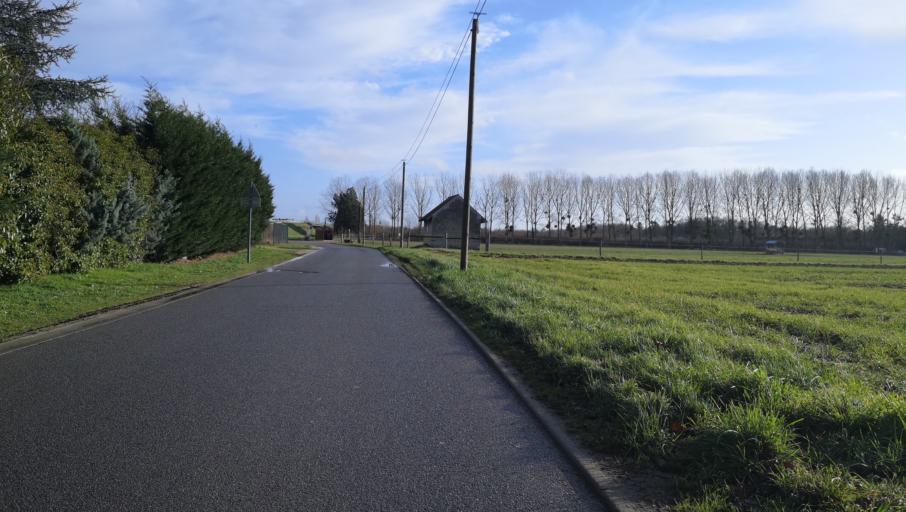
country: FR
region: Centre
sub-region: Departement du Loiret
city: Saint-Pryve-Saint-Mesmin
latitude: 47.8763
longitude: 1.8574
